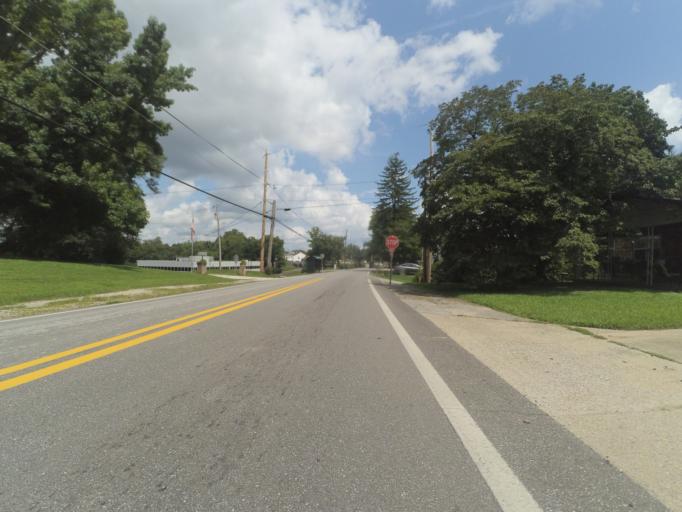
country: US
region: West Virginia
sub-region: Cabell County
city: Pea Ridge
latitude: 38.4093
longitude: -82.3443
